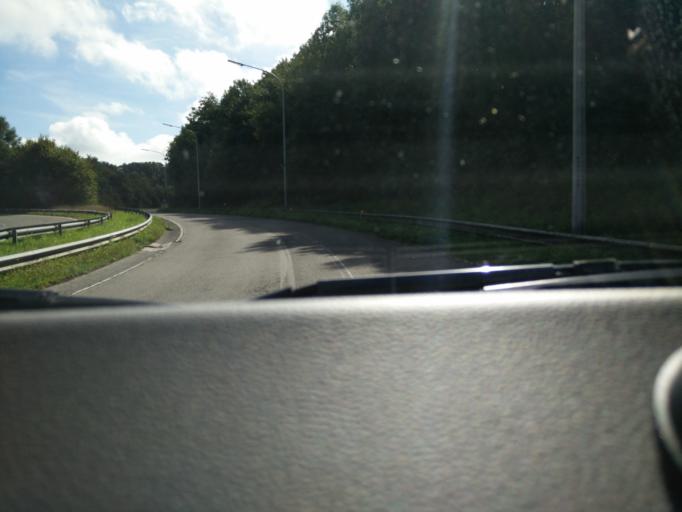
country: BE
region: Wallonia
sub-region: Province de Namur
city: Ciney
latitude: 50.2655
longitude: 5.0346
